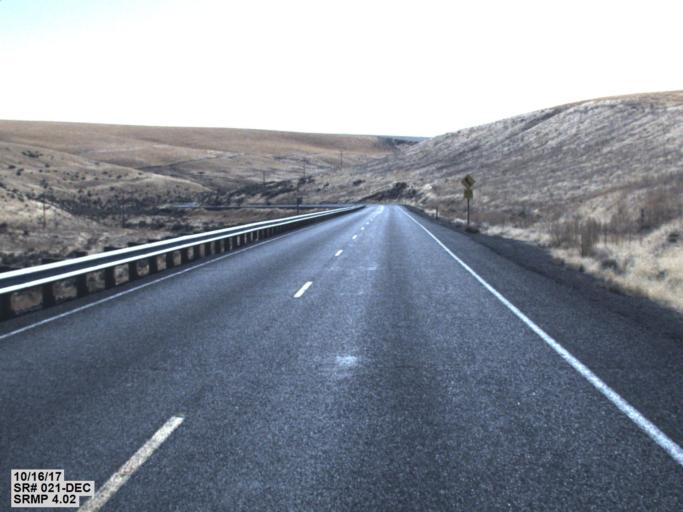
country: US
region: Washington
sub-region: Franklin County
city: Connell
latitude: 46.6953
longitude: -118.5287
